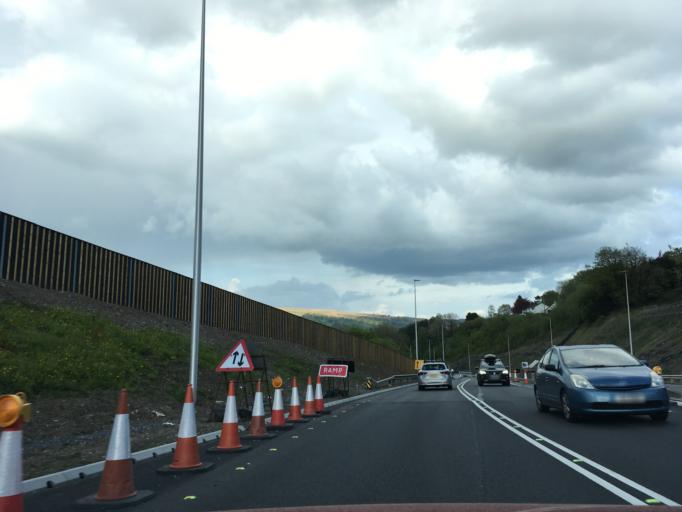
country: GB
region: Wales
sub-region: Monmouthshire
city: Gilwern
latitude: 51.8205
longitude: -3.1041
